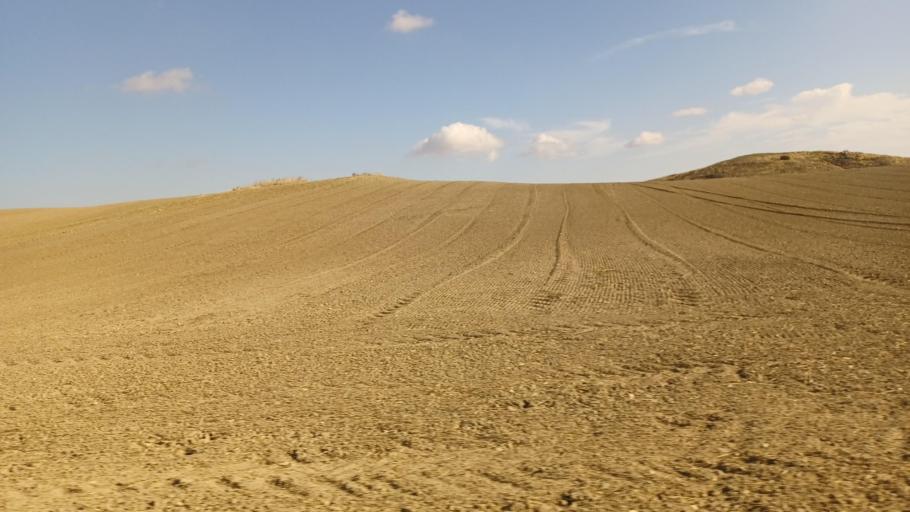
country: CY
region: Larnaka
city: Troulloi
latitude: 35.0234
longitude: 33.5839
